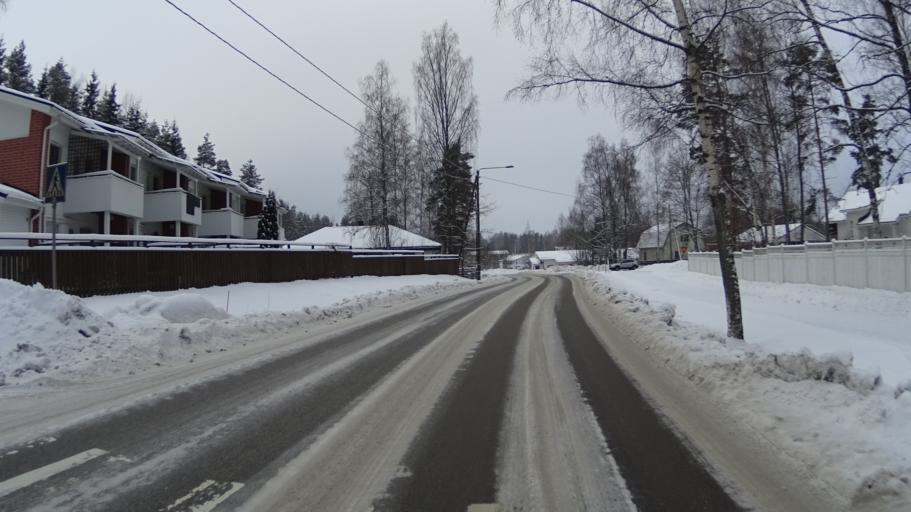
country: FI
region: Uusimaa
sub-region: Helsinki
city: Vihti
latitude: 60.3409
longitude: 24.2985
